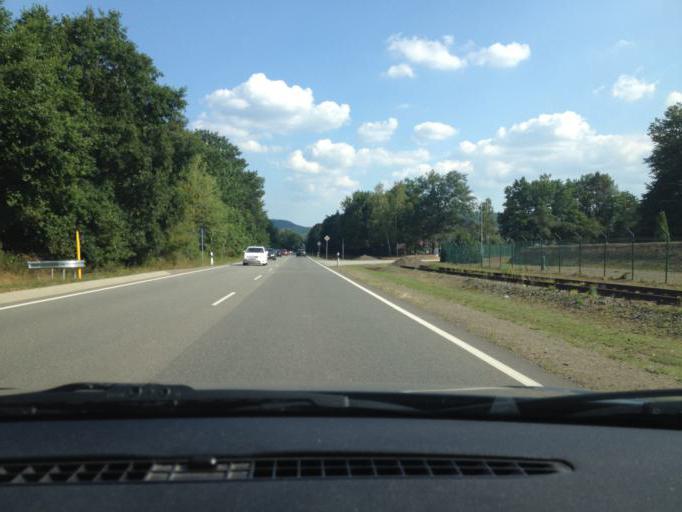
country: DE
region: Rheinland-Pfalz
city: Kindsbach
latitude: 49.4454
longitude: 7.6199
